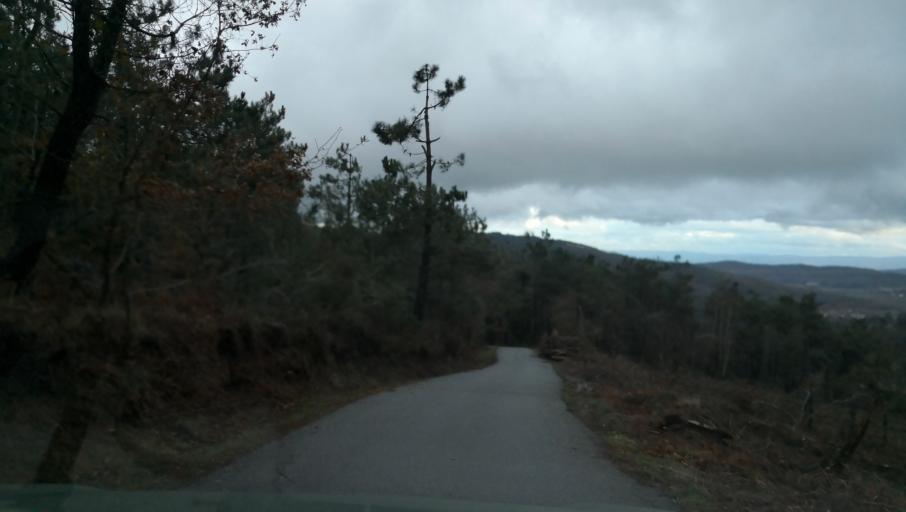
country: PT
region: Vila Real
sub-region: Mondim de Basto
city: Mondim de Basto
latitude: 41.3151
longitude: -7.8835
